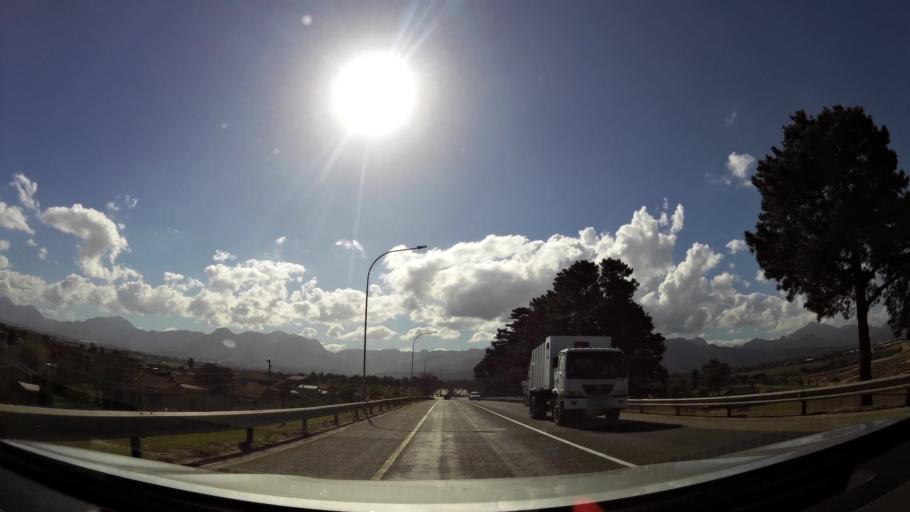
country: ZA
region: Western Cape
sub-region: Eden District Municipality
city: George
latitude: -33.9851
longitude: 22.4414
